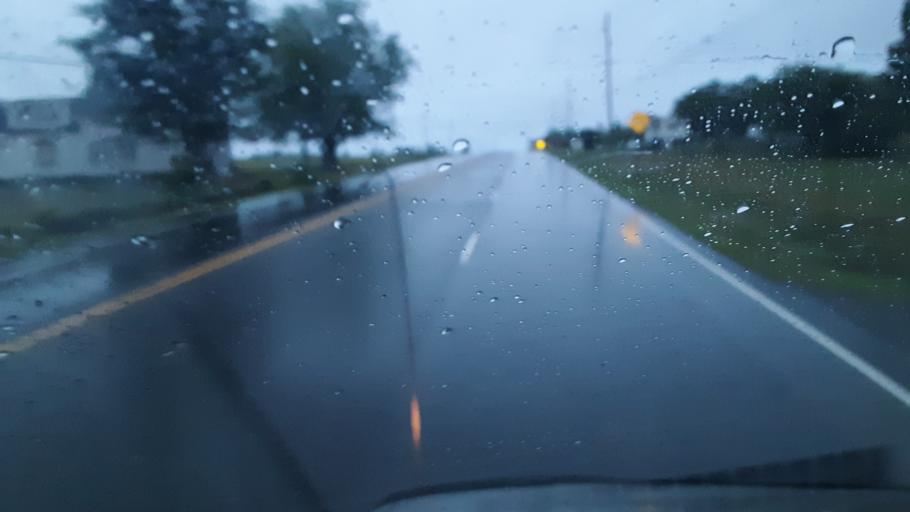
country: US
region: Maine
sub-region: Penobscot County
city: Patten
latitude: 45.9837
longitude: -68.4499
